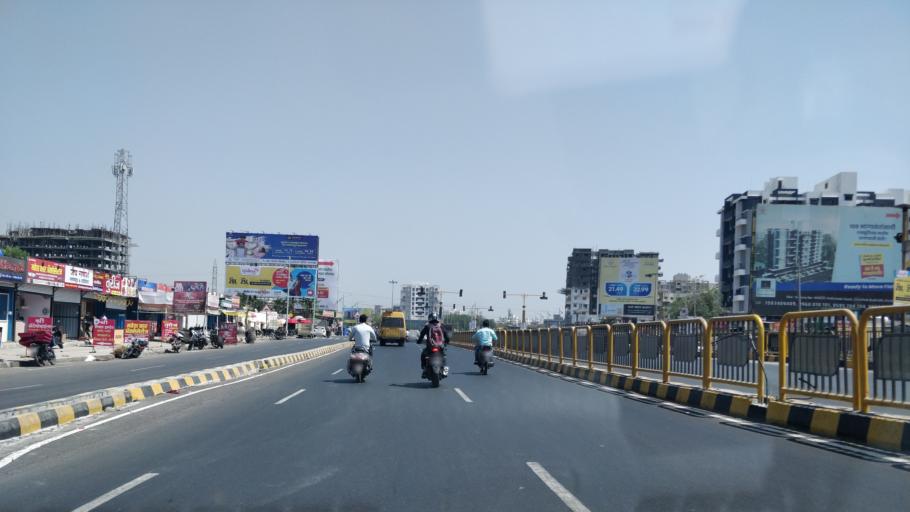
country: IN
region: Maharashtra
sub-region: Pune Division
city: Alandi
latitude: 18.6606
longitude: 73.8864
